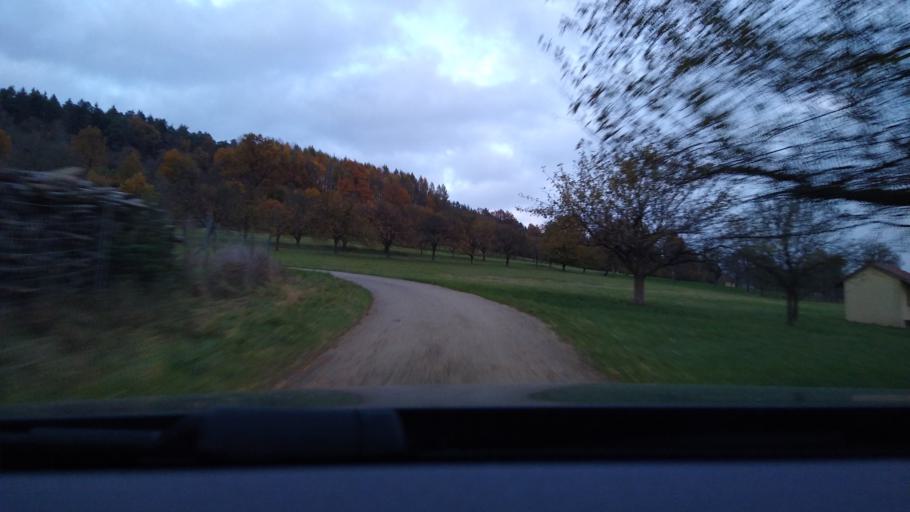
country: DE
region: Bavaria
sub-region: Upper Franconia
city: Igensdorf
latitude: 49.6295
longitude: 11.2386
